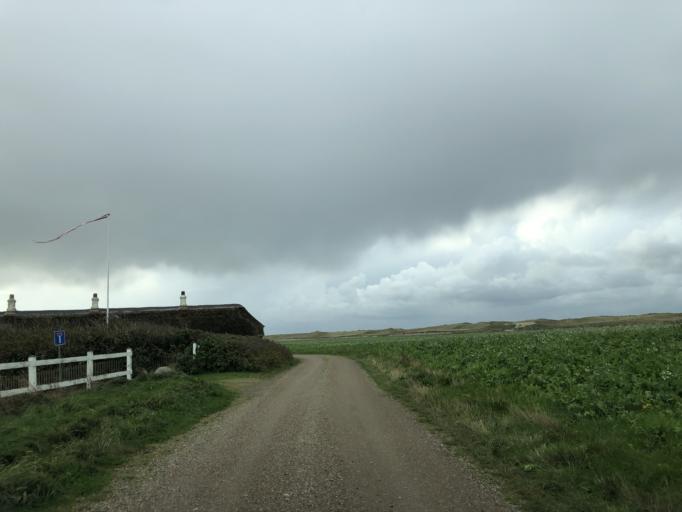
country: DK
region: Central Jutland
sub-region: Lemvig Kommune
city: Harboore
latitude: 56.4722
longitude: 8.1316
